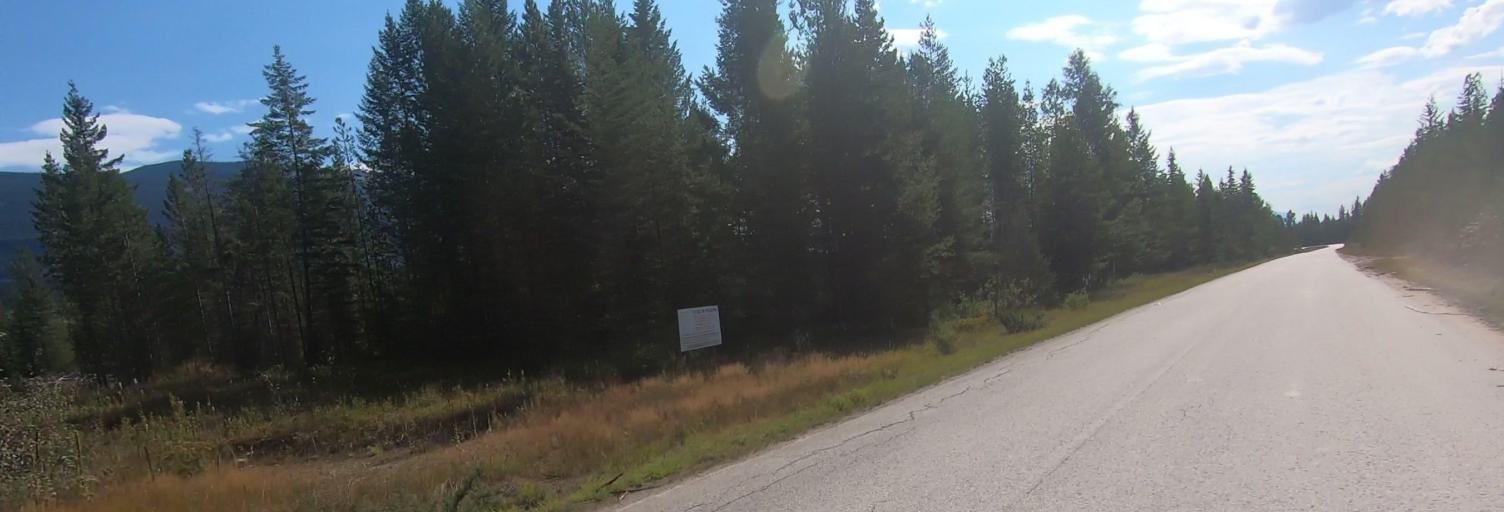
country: CA
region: British Columbia
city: Golden
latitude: 51.4912
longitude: -117.1744
